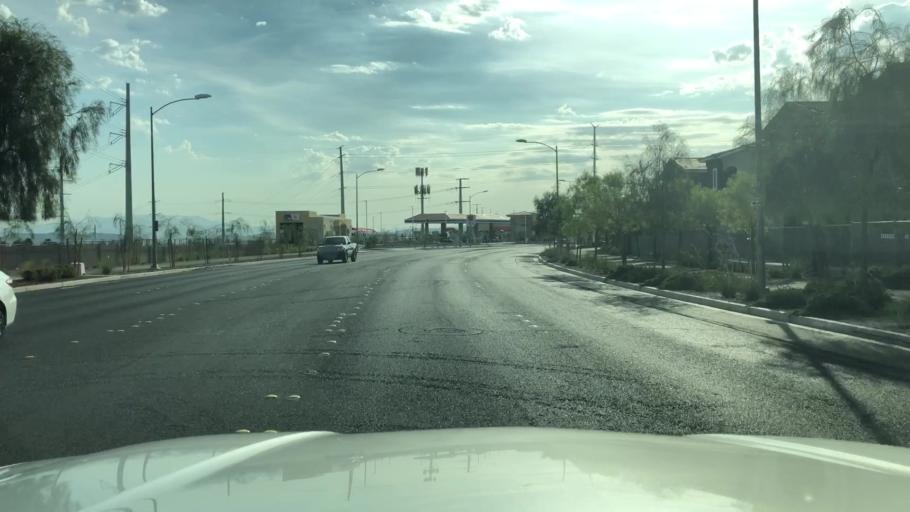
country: US
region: Nevada
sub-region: Clark County
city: Henderson
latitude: 36.0336
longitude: -115.0324
